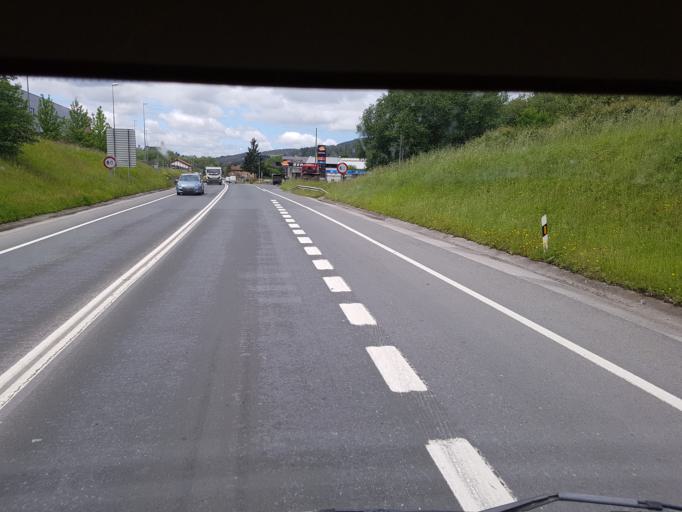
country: ES
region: Basque Country
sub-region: Bizkaia
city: Amorebieta
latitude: 43.2285
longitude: -2.7515
